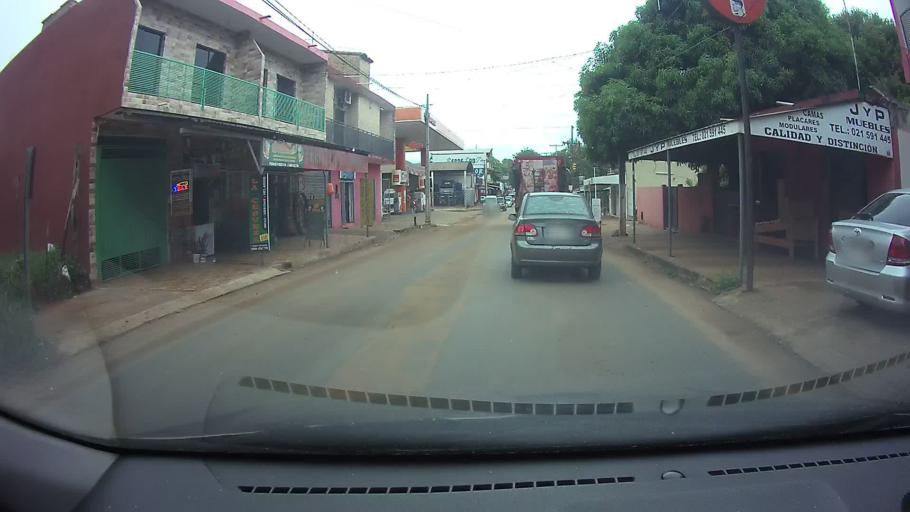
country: PY
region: Central
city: San Lorenzo
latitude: -25.3260
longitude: -57.5021
